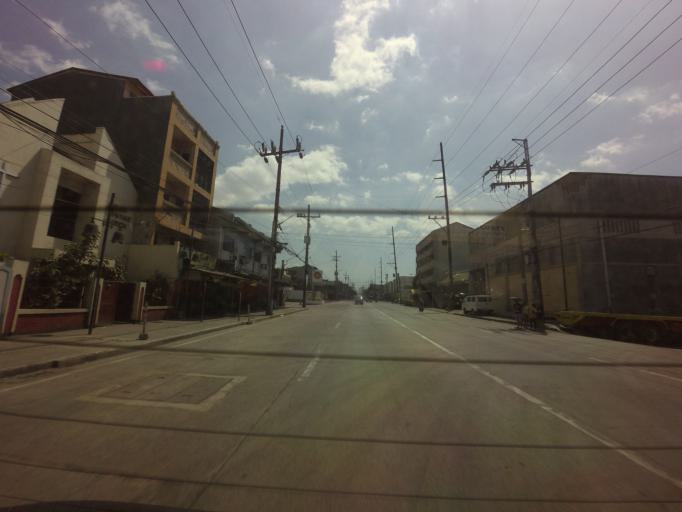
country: PH
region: Metro Manila
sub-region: Caloocan City
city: Niugan
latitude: 14.6329
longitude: 120.9633
